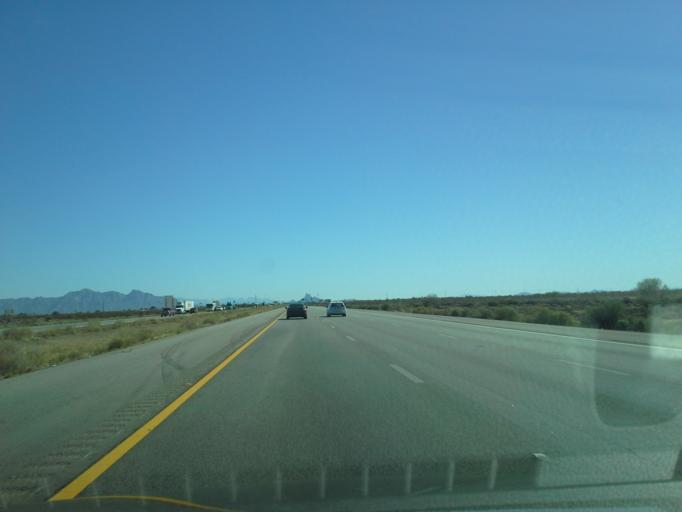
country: US
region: Arizona
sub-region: Pinal County
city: Arizona City
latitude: 32.7935
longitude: -111.6459
